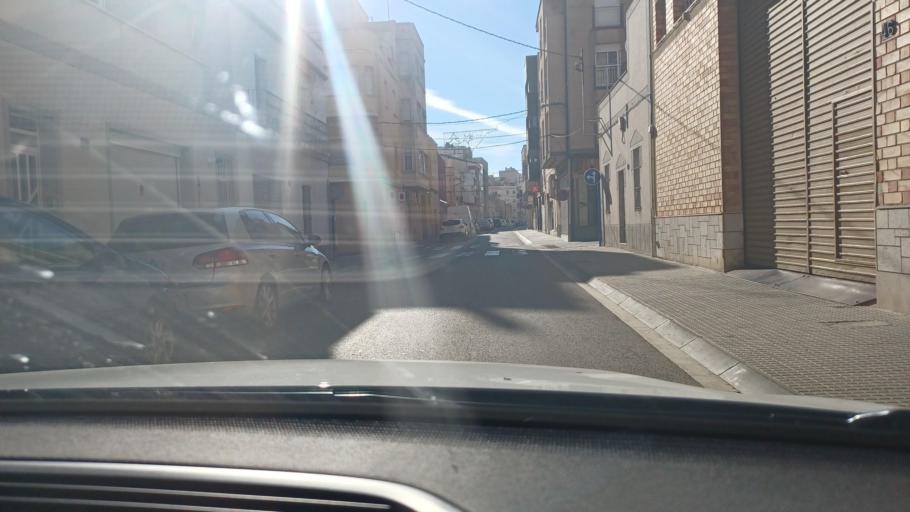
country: ES
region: Catalonia
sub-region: Provincia de Tarragona
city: Amposta
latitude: 40.7127
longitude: 0.5780
